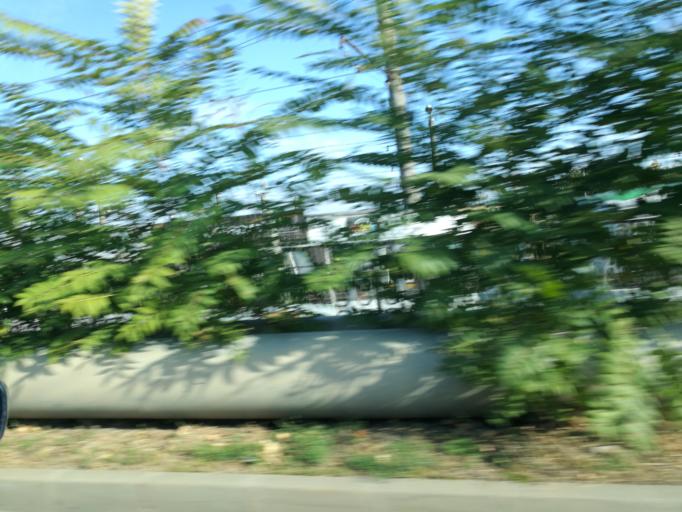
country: RO
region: Bihor
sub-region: Comuna Biharea
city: Oradea
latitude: 47.0384
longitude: 21.9383
